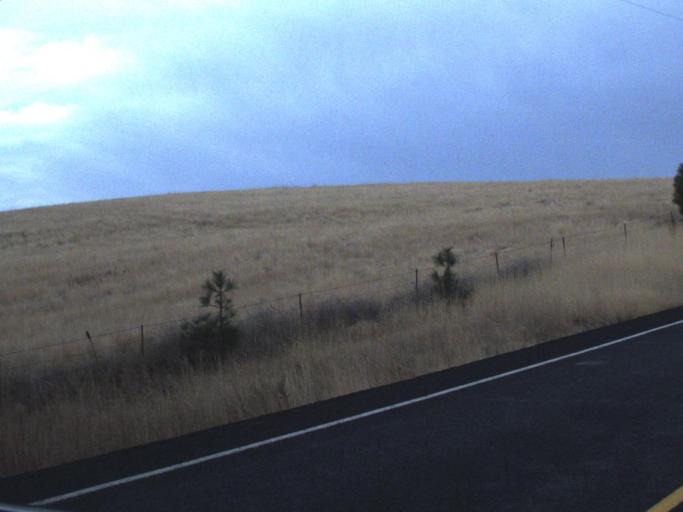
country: US
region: Washington
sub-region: Lincoln County
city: Davenport
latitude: 47.8118
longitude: -118.1798
